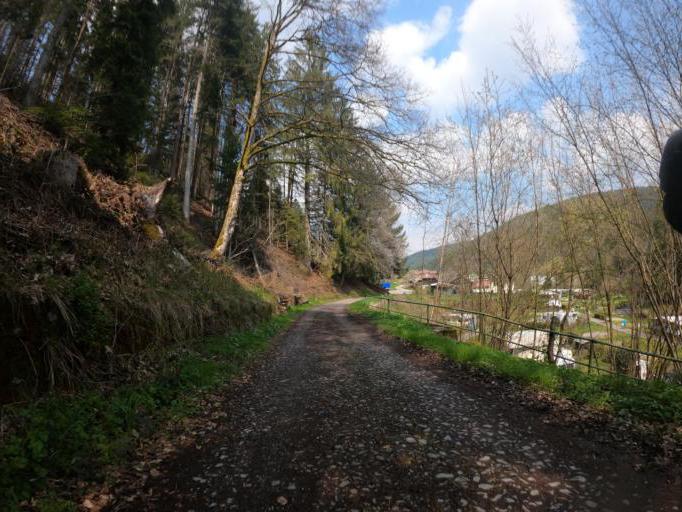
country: DE
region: Baden-Wuerttemberg
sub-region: Karlsruhe Region
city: Bad Wildbad
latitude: 48.7349
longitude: 8.5729
